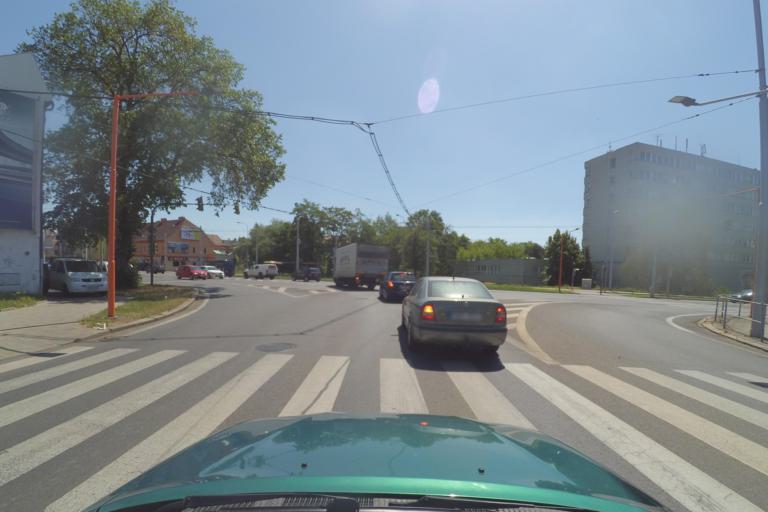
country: CZ
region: Ustecky
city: Novosedlice
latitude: 50.6508
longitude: 13.8377
